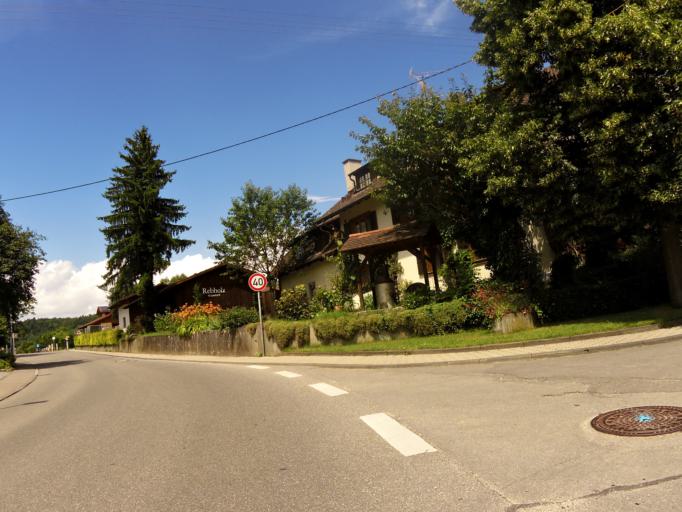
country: DE
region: Baden-Wuerttemberg
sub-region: Freiburg Region
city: Bodman-Ludwigshafen
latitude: 47.7760
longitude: 9.0266
